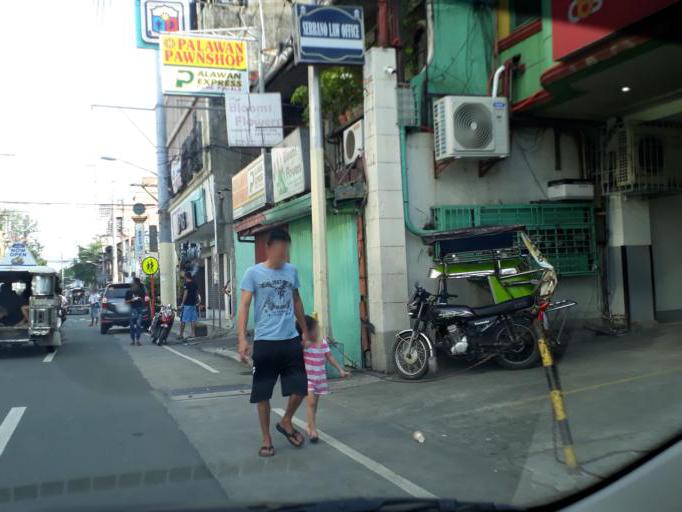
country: PH
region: Metro Manila
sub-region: Caloocan City
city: Niugan
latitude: 14.6500
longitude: 120.9729
